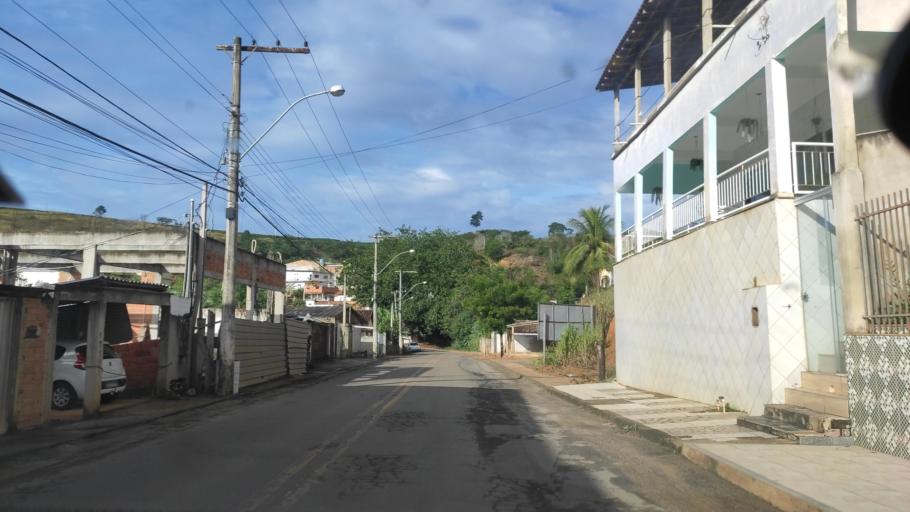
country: BR
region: Espirito Santo
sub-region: Nova Venecia
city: Nova Venecia
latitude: -18.7152
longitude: -40.3891
